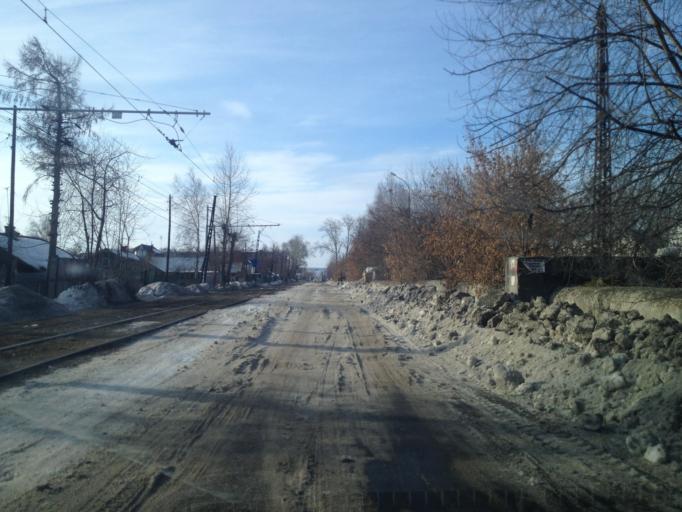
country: RU
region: Sverdlovsk
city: Sovkhoznyy
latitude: 56.7682
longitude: 60.5953
